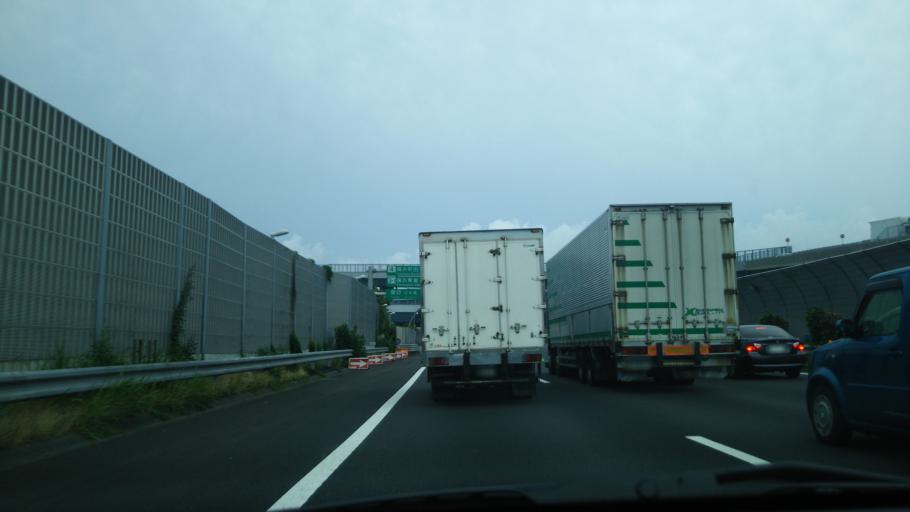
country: JP
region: Kanagawa
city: Atsugi
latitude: 35.4226
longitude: 139.3757
